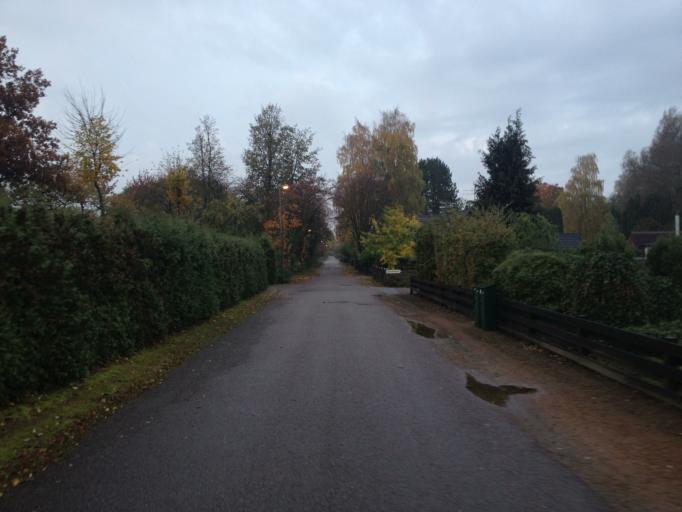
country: SE
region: Skane
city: Bjarred
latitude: 55.7305
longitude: 13.0281
